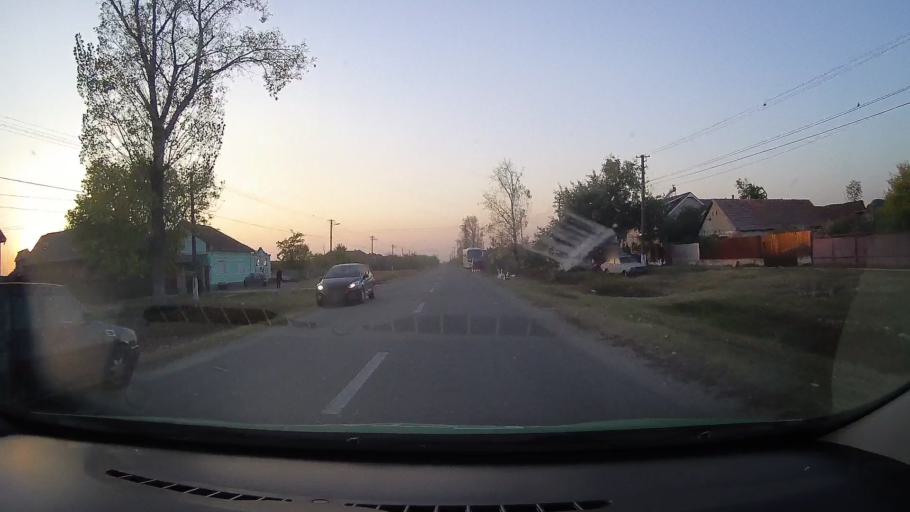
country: RO
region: Arad
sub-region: Comuna Zarand
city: Zarand
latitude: 46.4031
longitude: 21.6457
